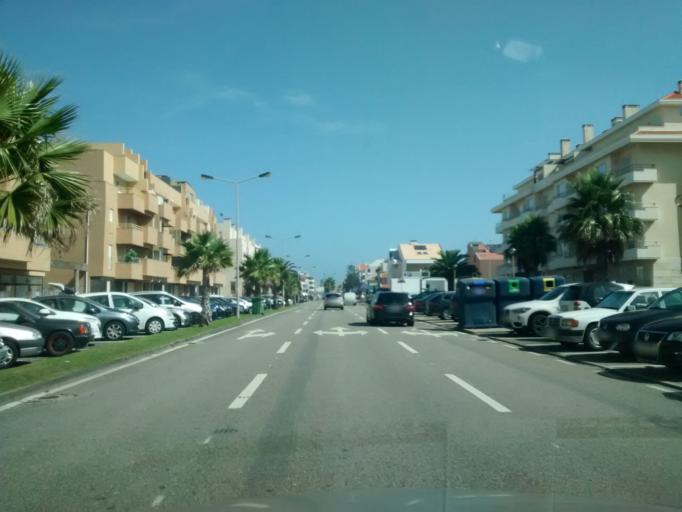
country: PT
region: Aveiro
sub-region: Ilhavo
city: Gafanha da Encarnacao
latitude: 40.6340
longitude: -8.7460
